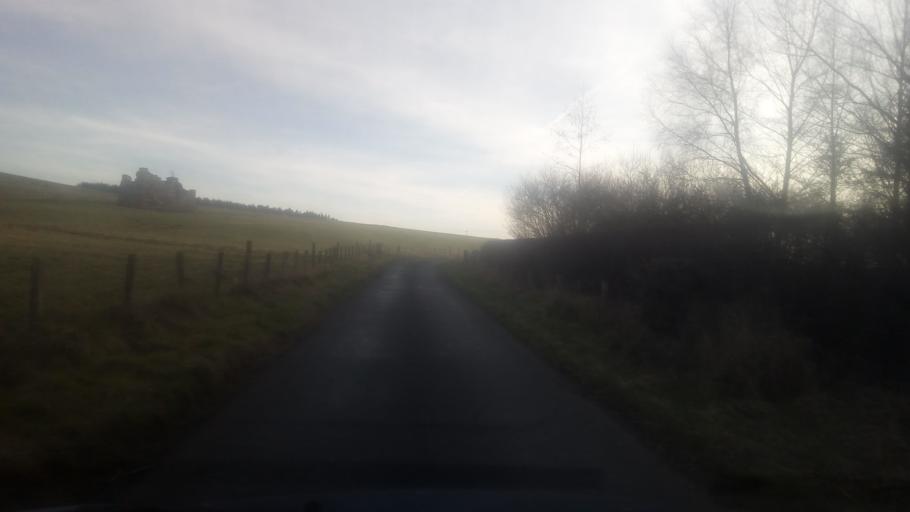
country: GB
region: Scotland
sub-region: The Scottish Borders
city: Jedburgh
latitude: 55.4357
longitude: -2.6254
